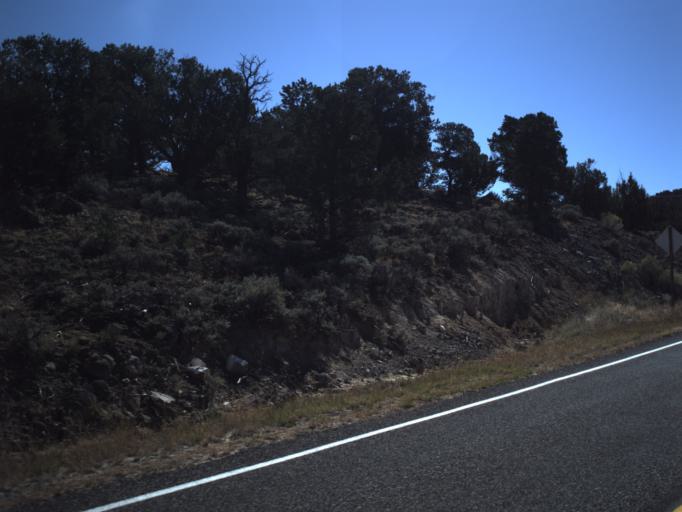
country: US
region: Utah
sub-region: Wayne County
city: Loa
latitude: 38.2420
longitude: -111.3772
